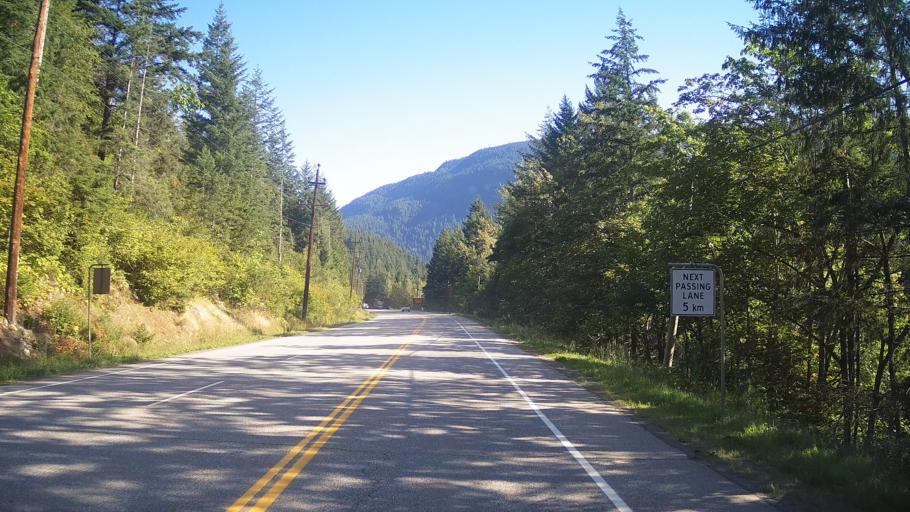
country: CA
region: British Columbia
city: Hope
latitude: 49.6834
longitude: -121.4163
